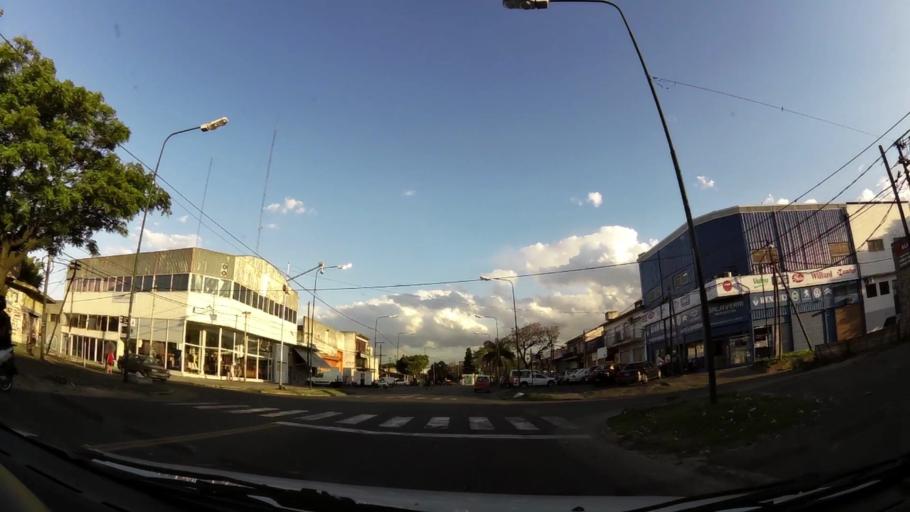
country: AR
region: Buenos Aires
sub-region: Partido de San Isidro
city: San Isidro
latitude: -34.4671
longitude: -58.5425
